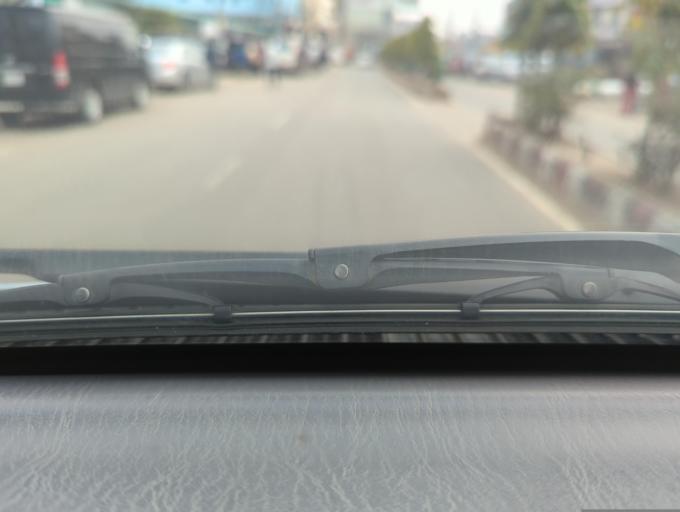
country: BD
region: Sylhet
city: Maulavi Bazar
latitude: 24.4888
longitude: 91.7629
